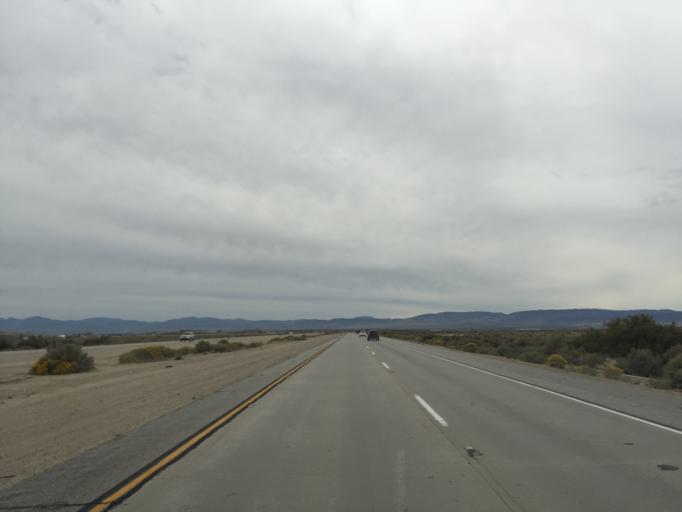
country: US
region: California
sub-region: Kern County
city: Rosamond
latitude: 34.7911
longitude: -118.1710
